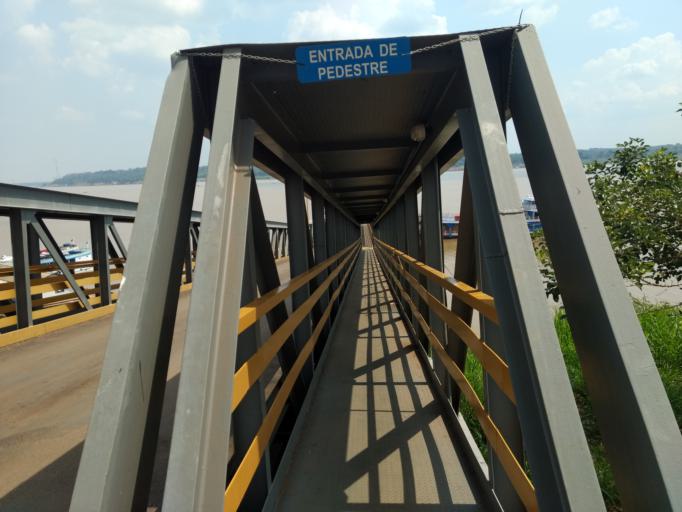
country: BR
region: Rondonia
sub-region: Porto Velho
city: Porto Velho
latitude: -8.7700
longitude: -63.9091
